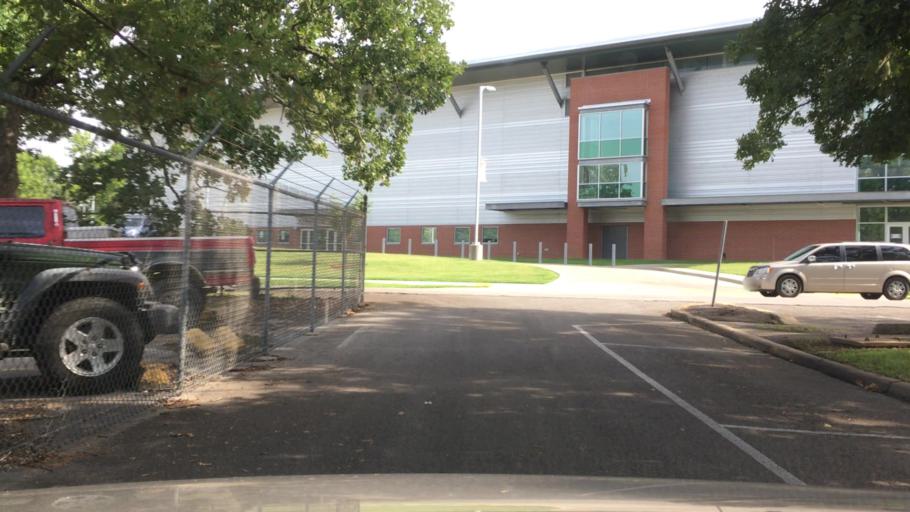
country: US
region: Oklahoma
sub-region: Cherokee County
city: Tahlequah
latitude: 35.9259
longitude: -94.9678
